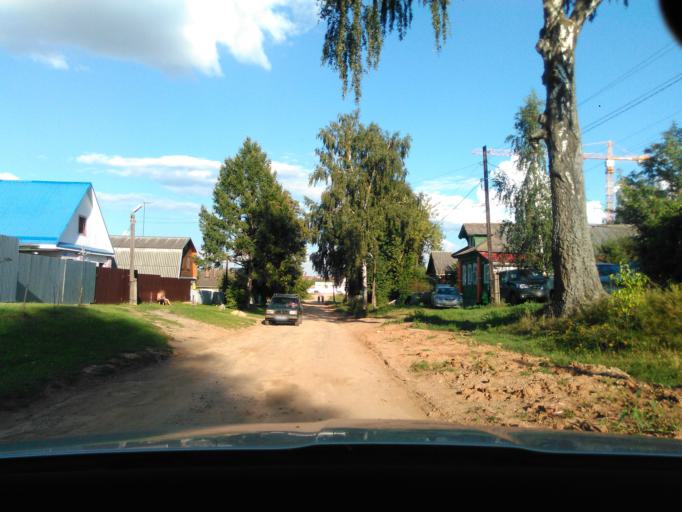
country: RU
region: Tverskaya
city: Zavidovo
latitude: 56.5813
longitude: 36.5166
